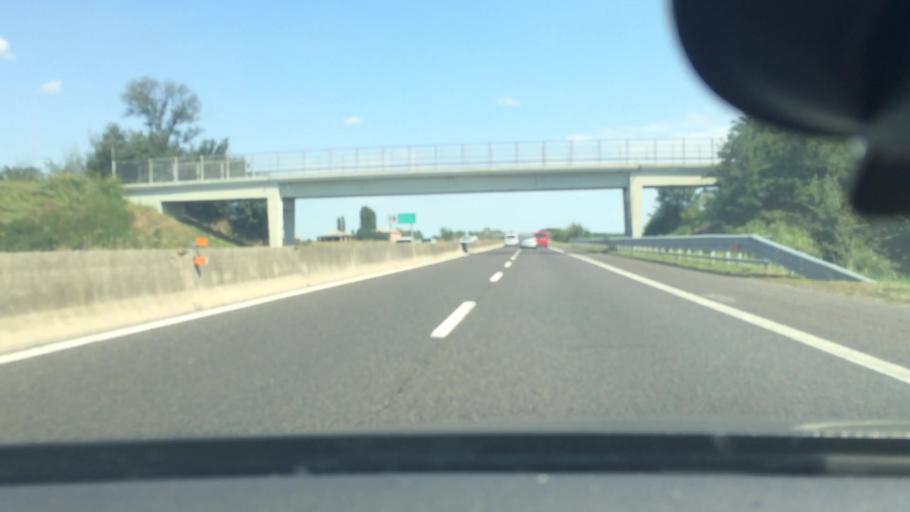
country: IT
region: Emilia-Romagna
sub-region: Provincia di Bologna
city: Malalbergo
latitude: 44.7464
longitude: 11.5269
